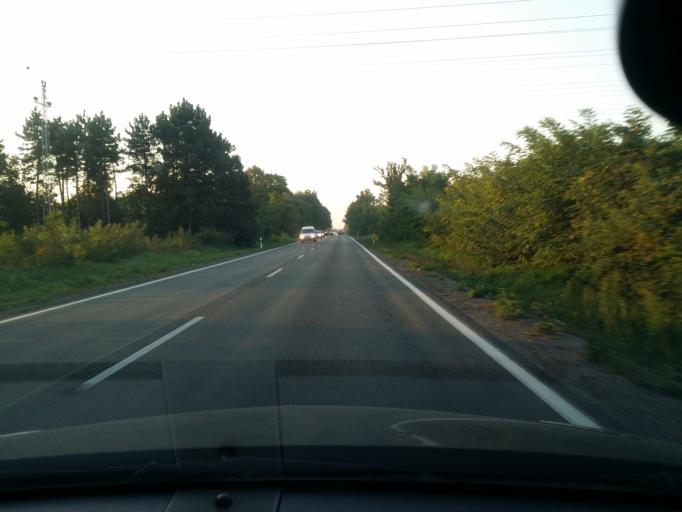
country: HU
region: Fejer
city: dunaujvaros
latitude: 46.9568
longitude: 18.9107
